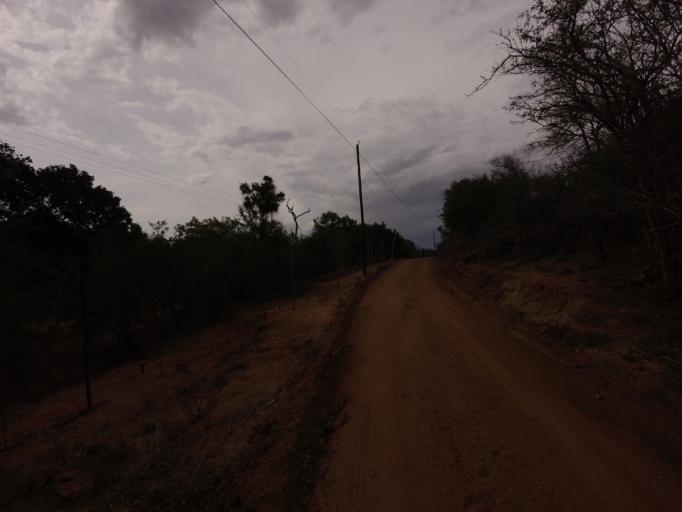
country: ZA
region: Limpopo
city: Thulamahashi
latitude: -24.5199
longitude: 31.1124
